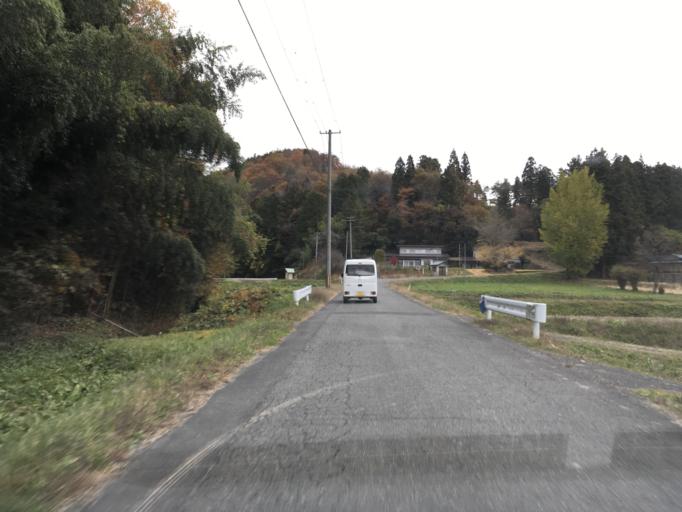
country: JP
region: Iwate
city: Mizusawa
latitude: 39.0474
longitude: 141.3327
